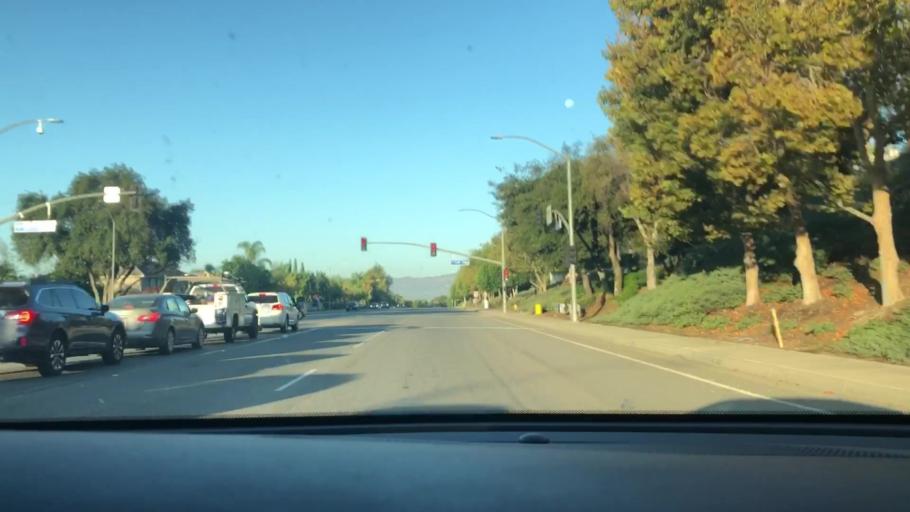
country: US
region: California
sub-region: Riverside County
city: Murrieta
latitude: 33.5957
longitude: -117.1969
